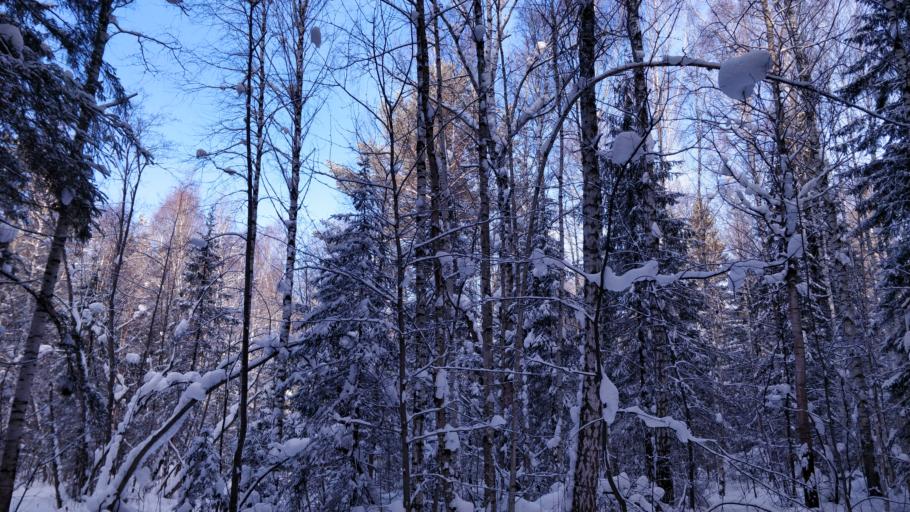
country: RU
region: Perm
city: Perm
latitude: 58.0615
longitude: 56.2216
